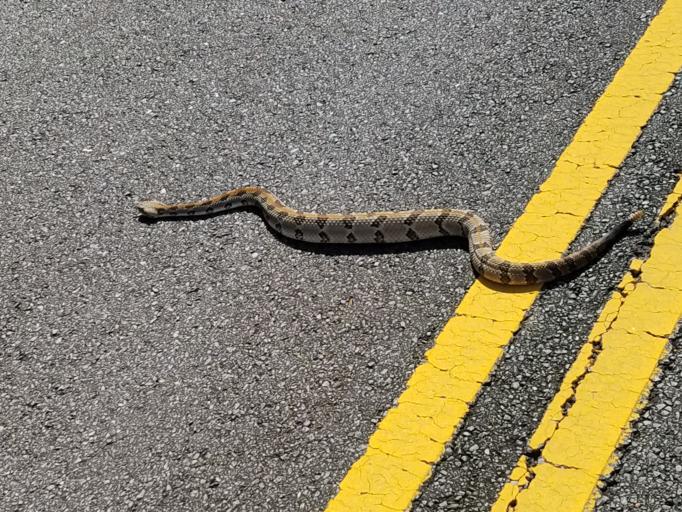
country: US
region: Oklahoma
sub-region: Le Flore County
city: Heavener
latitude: 34.7122
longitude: -94.6747
